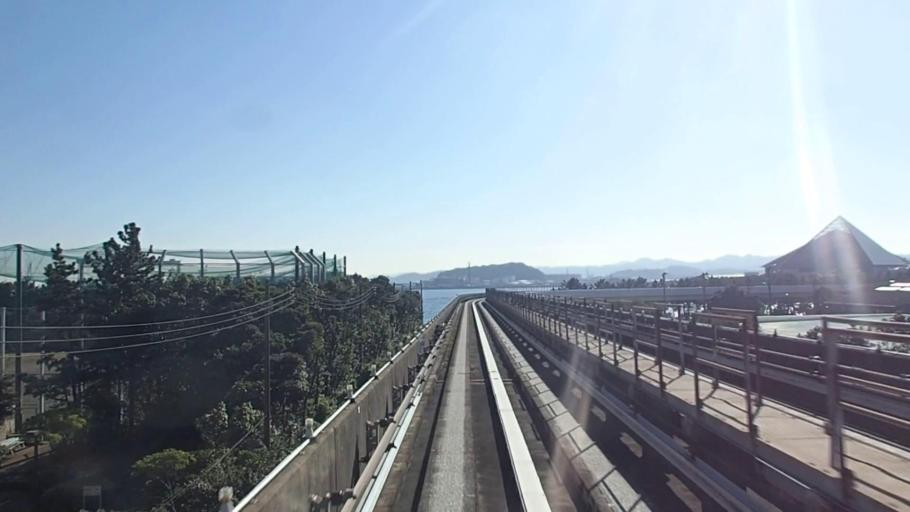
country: JP
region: Kanagawa
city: Yokosuka
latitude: 35.3425
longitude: 139.6502
